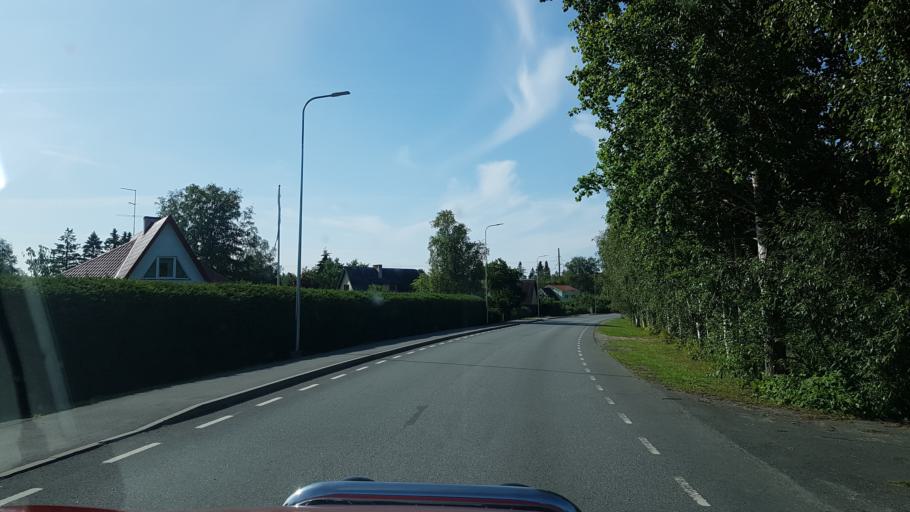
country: EE
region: Harju
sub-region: Joelaehtme vald
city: Loo
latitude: 59.3894
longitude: 24.9353
